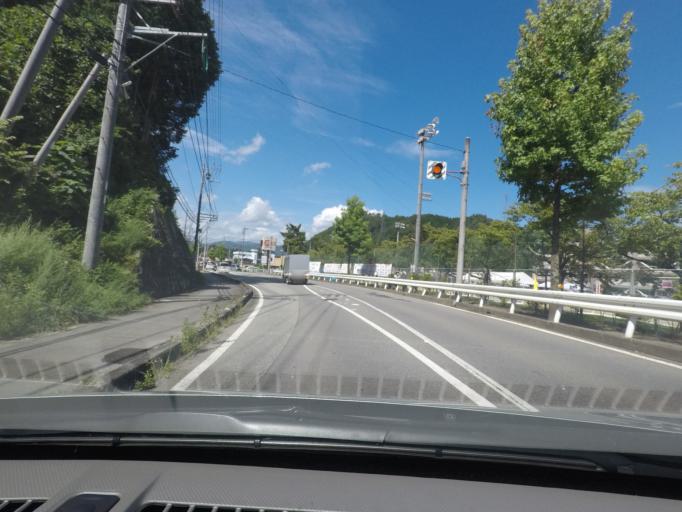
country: JP
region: Gifu
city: Takayama
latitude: 36.1505
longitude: 137.2741
